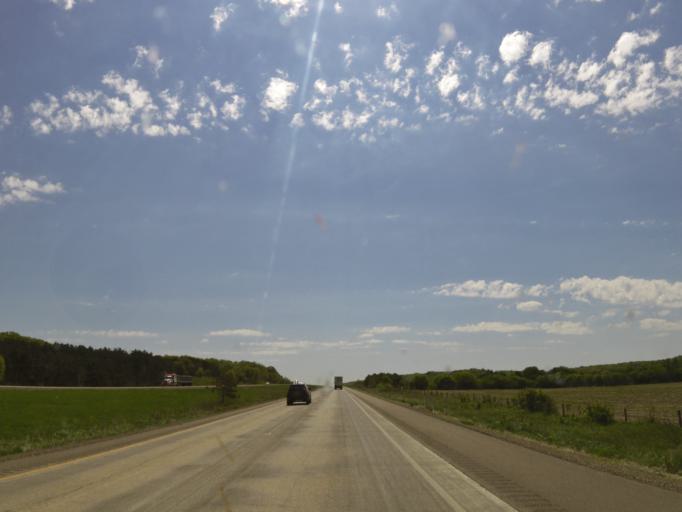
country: US
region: Wisconsin
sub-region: Trempealeau County
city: Osseo
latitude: 44.6174
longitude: -91.2488
